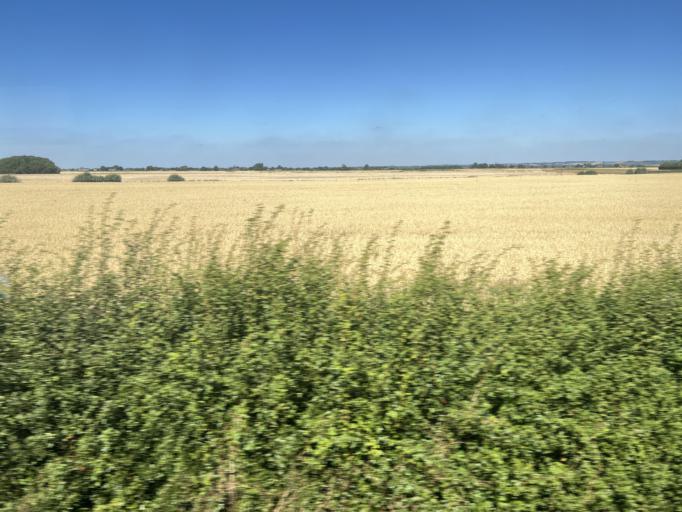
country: GB
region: England
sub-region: Lincolnshire
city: Spilsby
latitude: 53.0787
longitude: 0.0826
